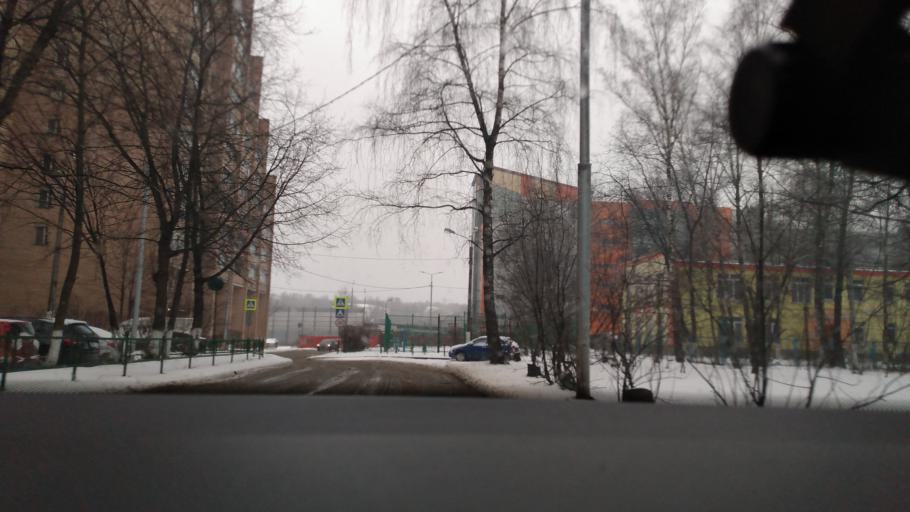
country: RU
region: Moskovskaya
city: Balashikha
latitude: 55.7967
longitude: 37.9509
